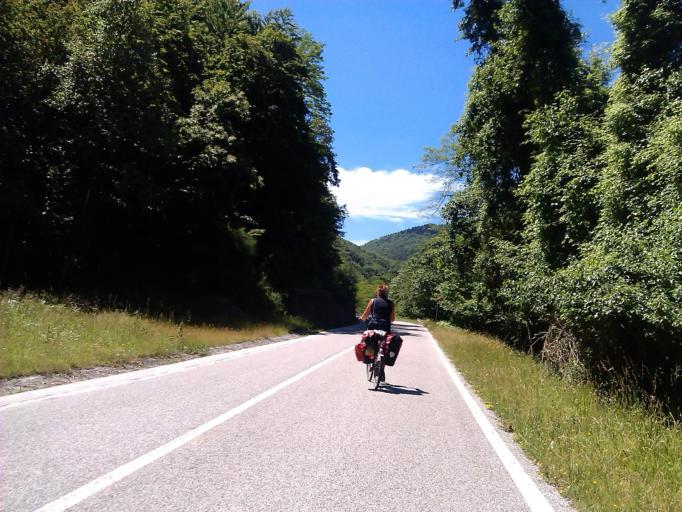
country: IT
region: Tuscany
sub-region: Provincia di Prato
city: Cantagallo
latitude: 44.0456
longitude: 11.0408
